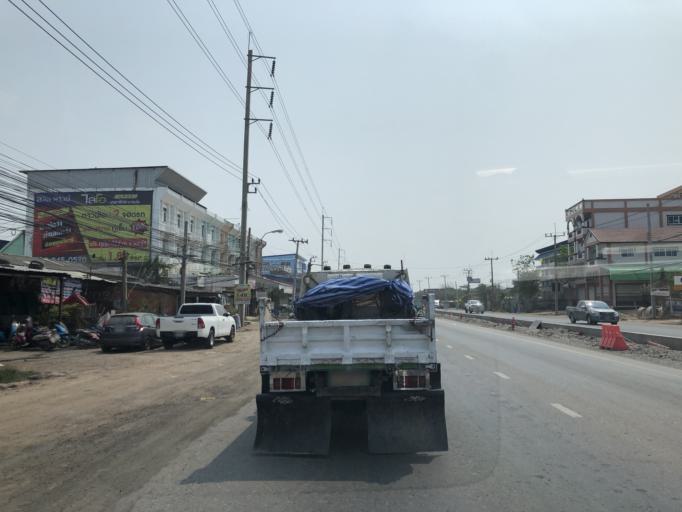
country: TH
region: Samut Prakan
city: Bang Bo
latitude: 13.5063
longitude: 100.8270
